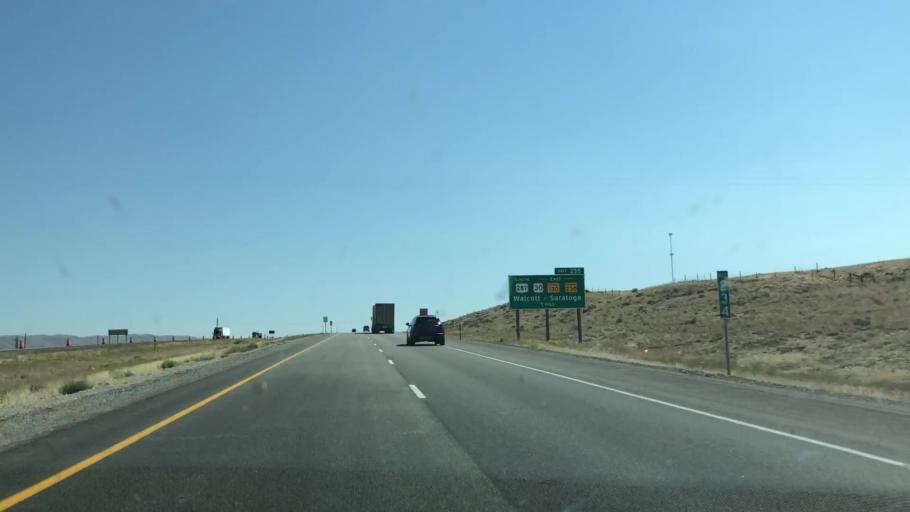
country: US
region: Wyoming
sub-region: Carbon County
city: Saratoga
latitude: 41.7420
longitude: -106.8543
